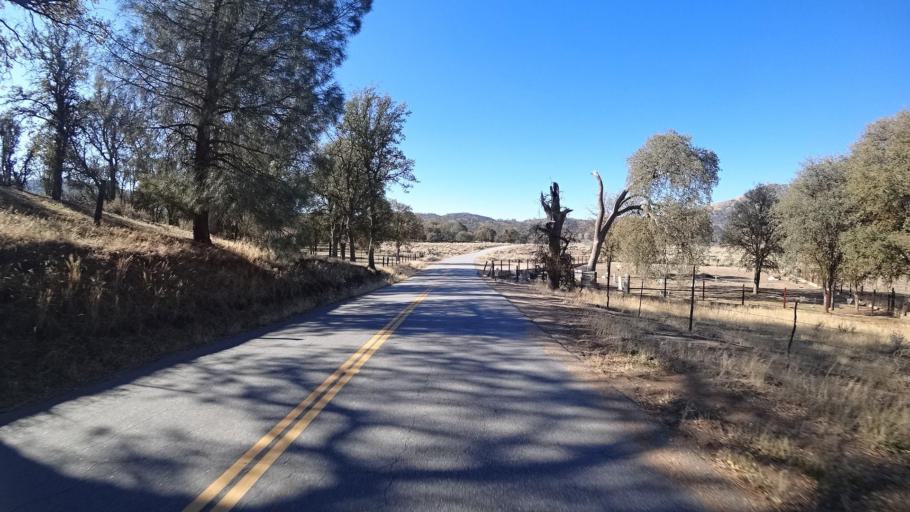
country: US
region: California
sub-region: Kern County
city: Bodfish
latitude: 35.3846
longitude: -118.5383
